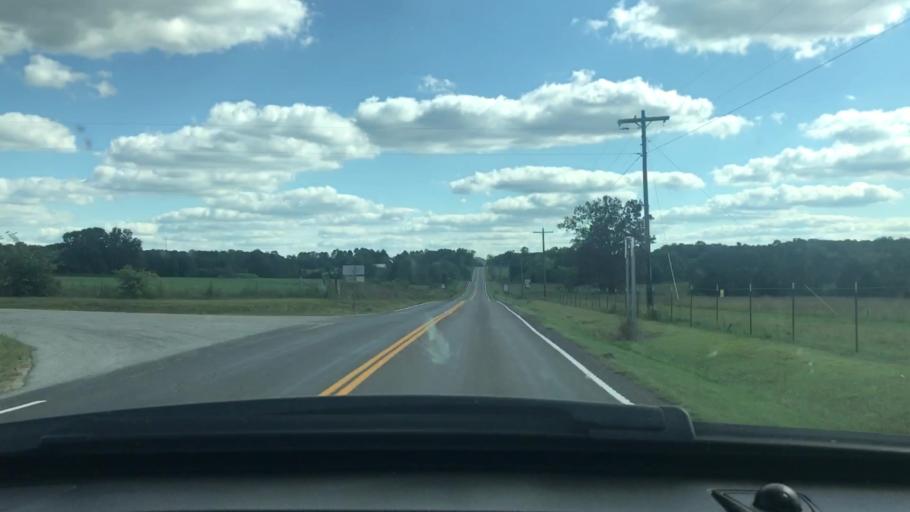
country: US
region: Missouri
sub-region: Wright County
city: Mountain Grove
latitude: 37.2428
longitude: -92.3004
